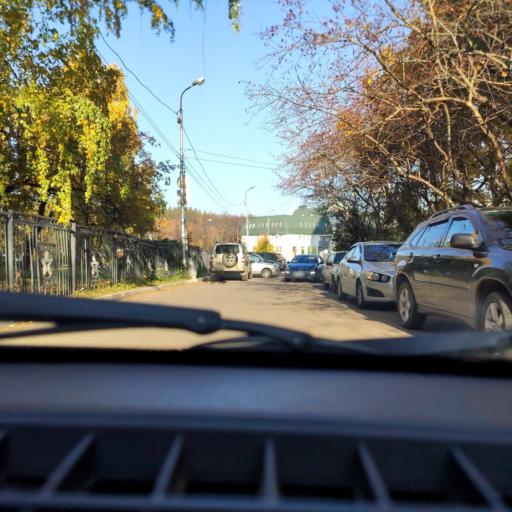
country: RU
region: Bashkortostan
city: Ufa
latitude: 54.7704
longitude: 56.0097
